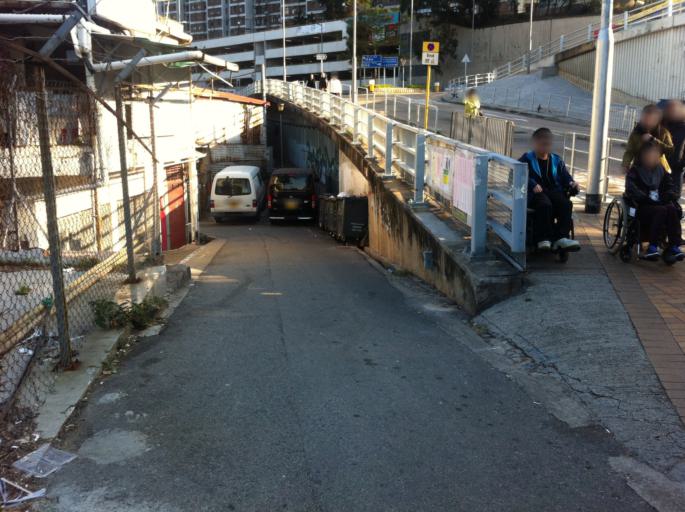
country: HK
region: Central and Western
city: Central
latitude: 22.2599
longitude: 114.1367
